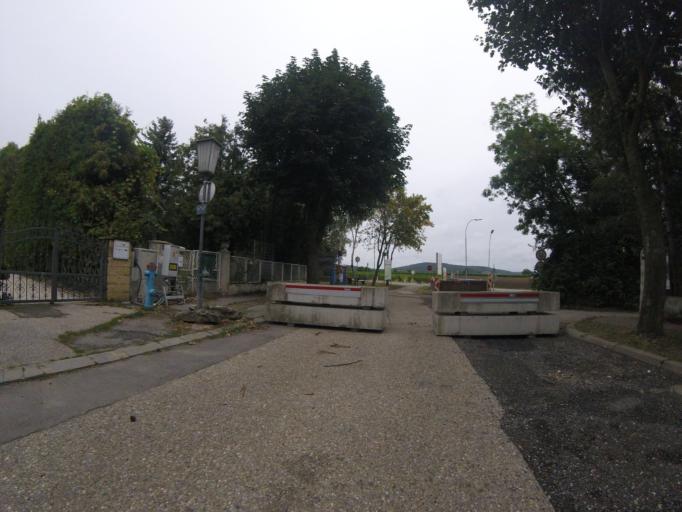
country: AT
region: Burgenland
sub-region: Politischer Bezirk Neusiedl am See
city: Winden am See
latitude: 47.9535
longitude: 16.7393
